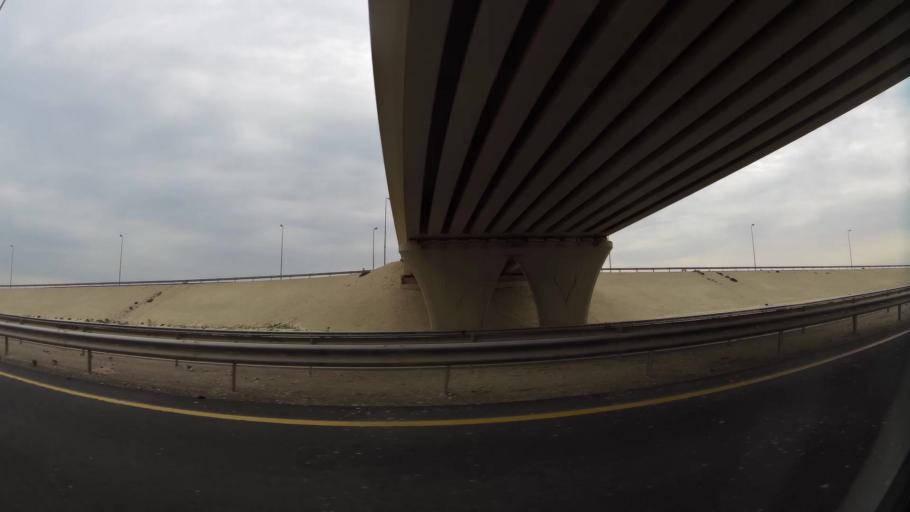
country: BH
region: Central Governorate
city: Dar Kulayb
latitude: 25.8866
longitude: 50.5773
